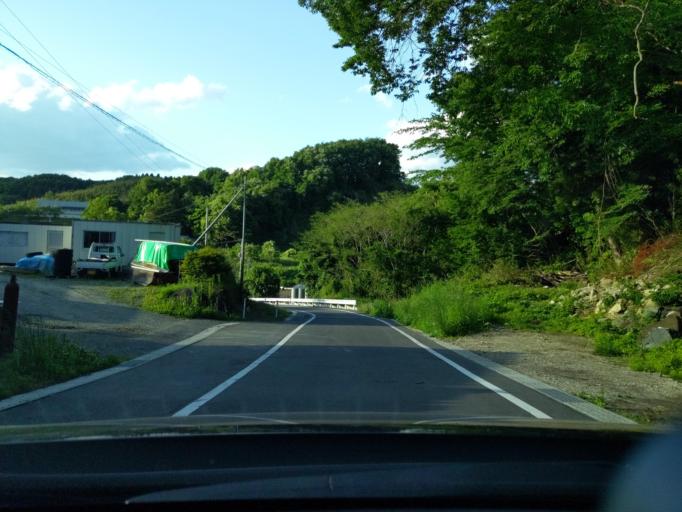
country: JP
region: Fukushima
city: Miharu
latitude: 37.4291
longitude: 140.4350
